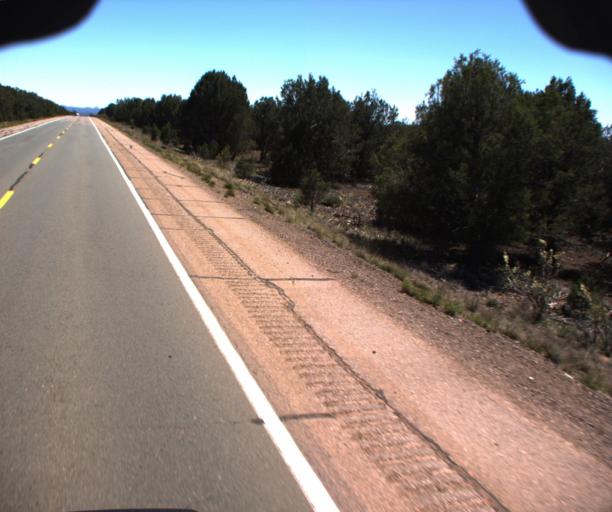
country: US
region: Arizona
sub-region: Yavapai County
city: Paulden
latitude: 35.0737
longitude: -112.4023
